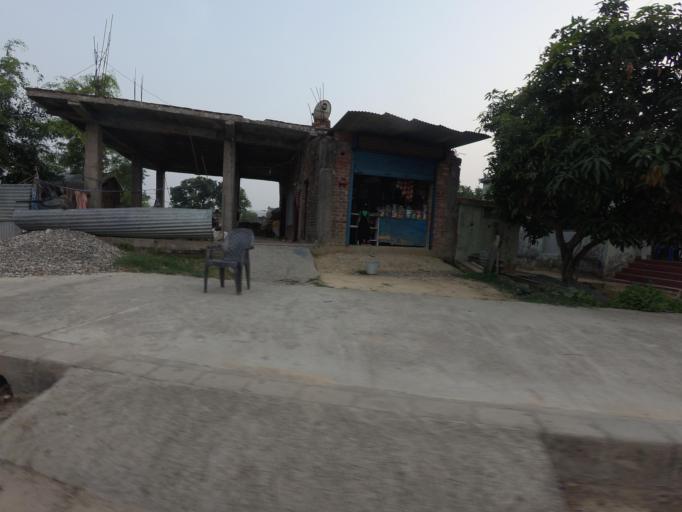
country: NP
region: Western Region
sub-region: Lumbini Zone
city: Bhairahawa
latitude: 27.4954
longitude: 83.4630
